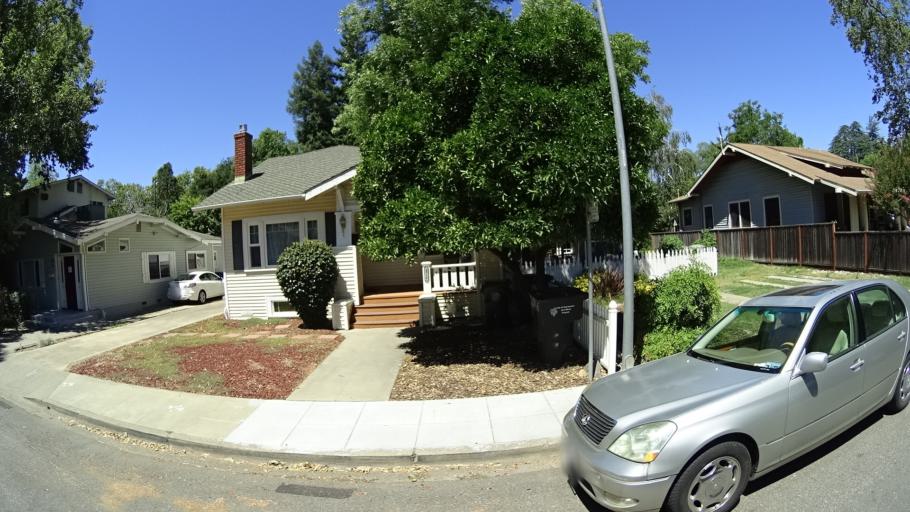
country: US
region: California
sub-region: Sacramento County
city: Sacramento
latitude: 38.5523
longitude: -121.4586
